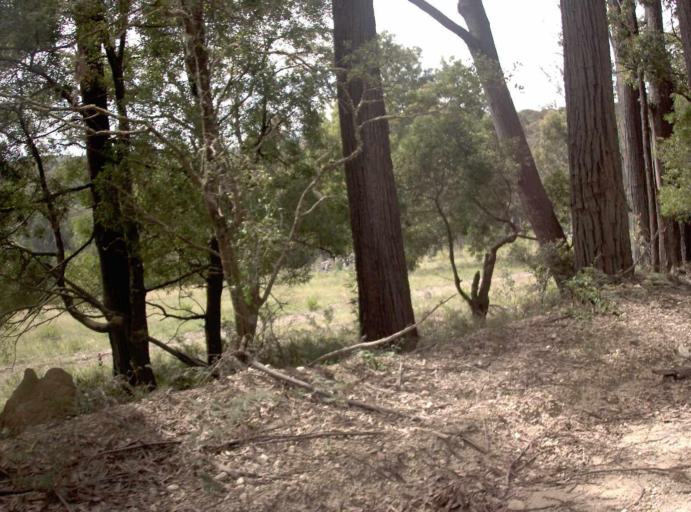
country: AU
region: Victoria
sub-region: East Gippsland
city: Lakes Entrance
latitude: -37.6287
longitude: 148.6760
